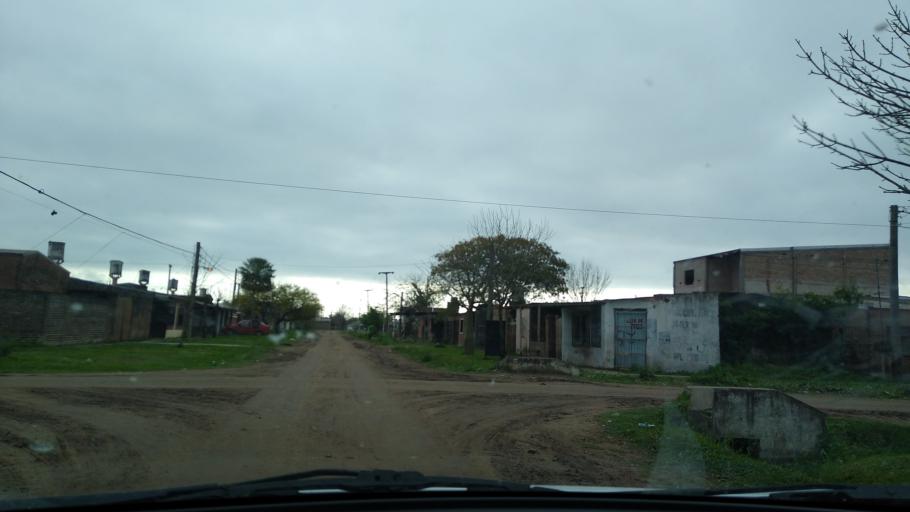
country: AR
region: Chaco
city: Resistencia
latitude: -27.4913
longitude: -58.9815
